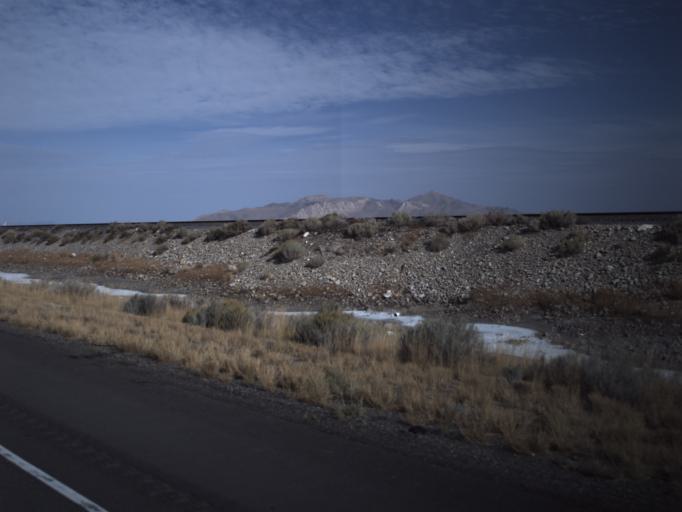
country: US
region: Utah
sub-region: Tooele County
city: Stansbury park
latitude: 40.6716
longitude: -112.3872
